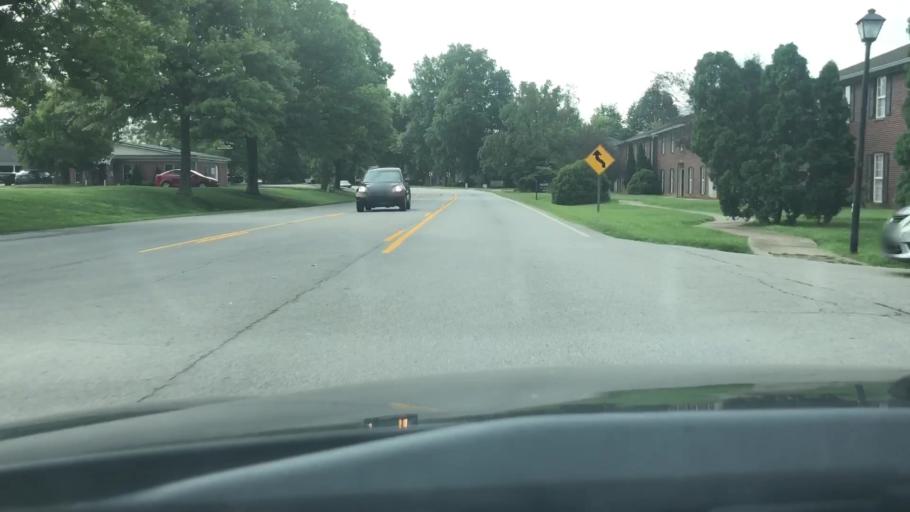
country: US
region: Kentucky
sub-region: Jefferson County
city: Graymoor-Devondale
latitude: 38.2668
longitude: -85.6127
